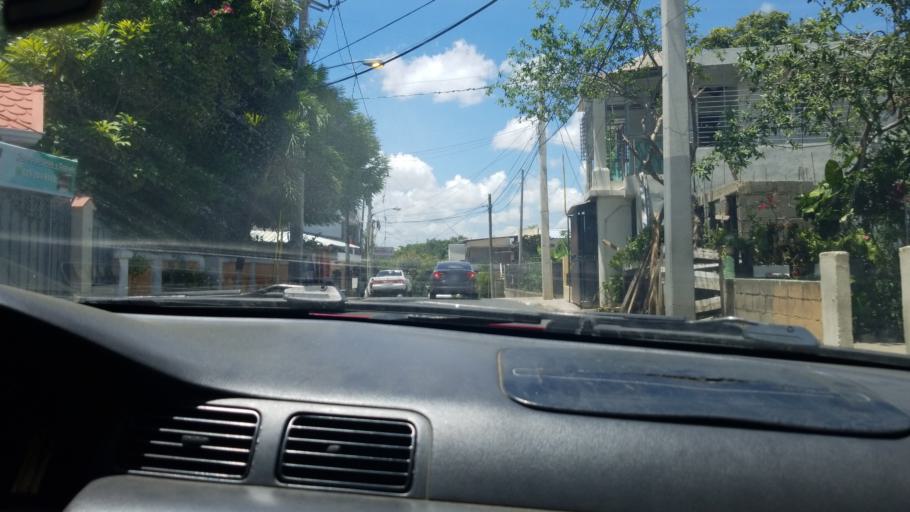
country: DO
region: Santiago
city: Santiago de los Caballeros
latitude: 19.4823
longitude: -70.6874
